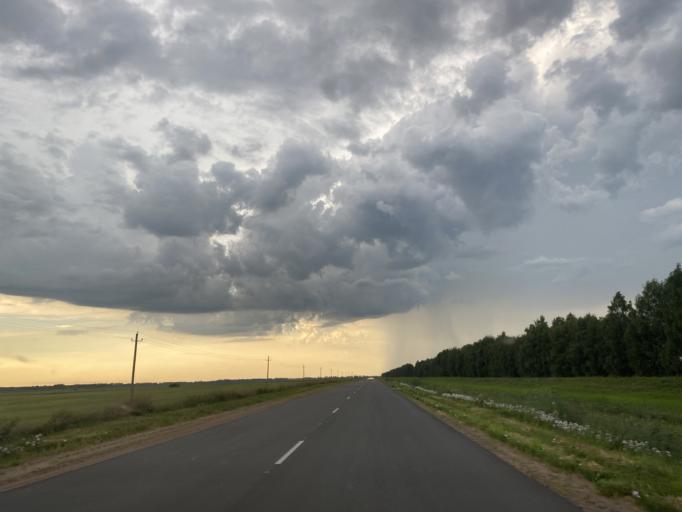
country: BY
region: Brest
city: Ivanava
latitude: 52.4219
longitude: 25.5712
